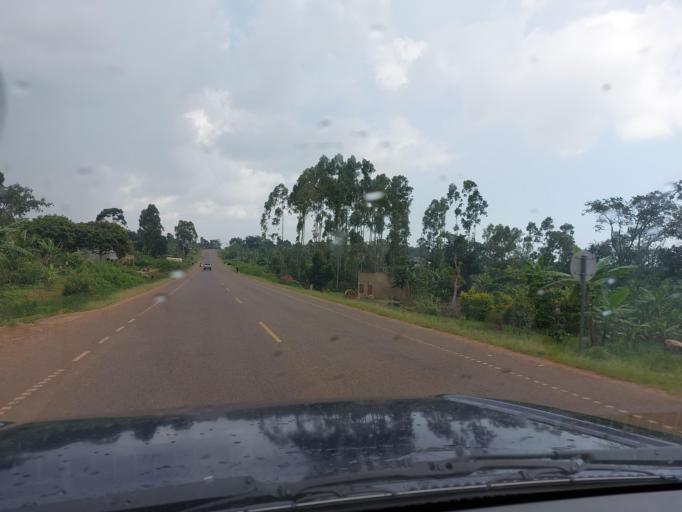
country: UG
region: Central Region
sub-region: Buikwe District
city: Buikwe
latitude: 0.2413
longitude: 32.9324
